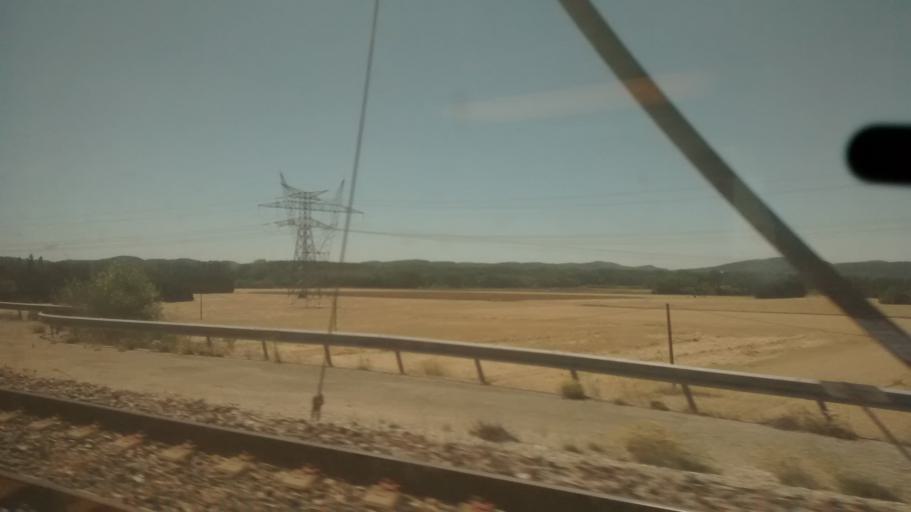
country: FR
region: Provence-Alpes-Cote d'Azur
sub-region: Departement du Vaucluse
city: Mondragon
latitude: 44.2460
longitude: 4.6915
